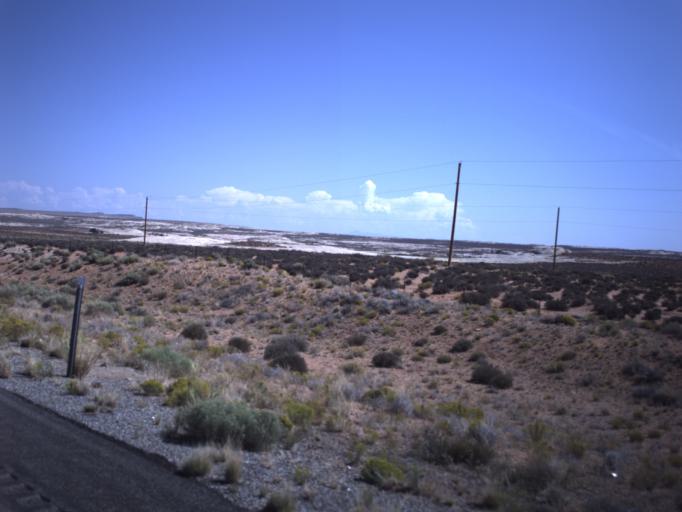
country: US
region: Utah
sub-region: San Juan County
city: Blanding
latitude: 37.0714
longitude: -109.5511
